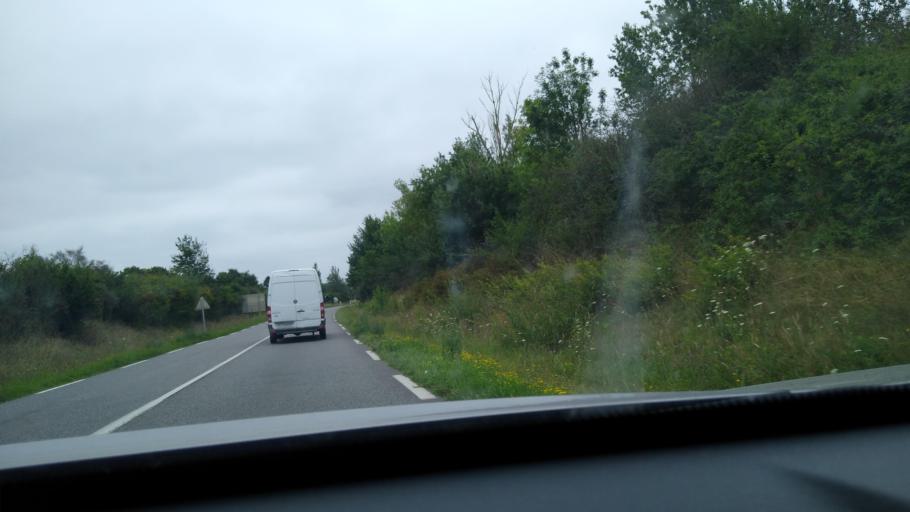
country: FR
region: Midi-Pyrenees
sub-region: Departement du Tarn
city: Brens
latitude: 43.8758
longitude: 1.9088
